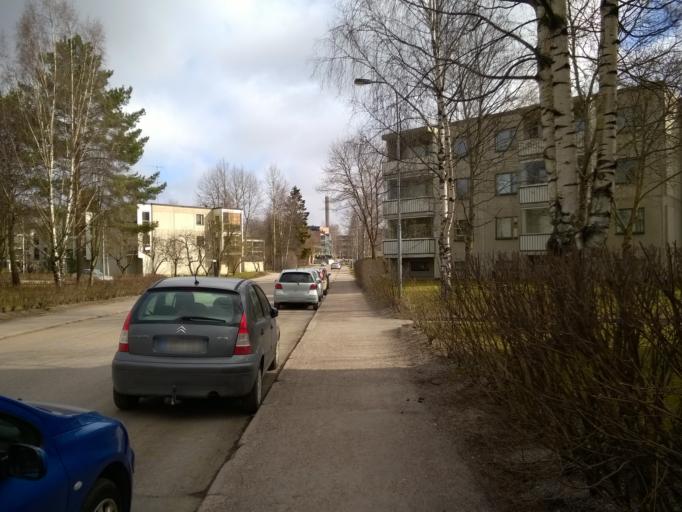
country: FI
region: Uusimaa
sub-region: Helsinki
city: Helsinki
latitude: 60.2312
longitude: 24.9702
